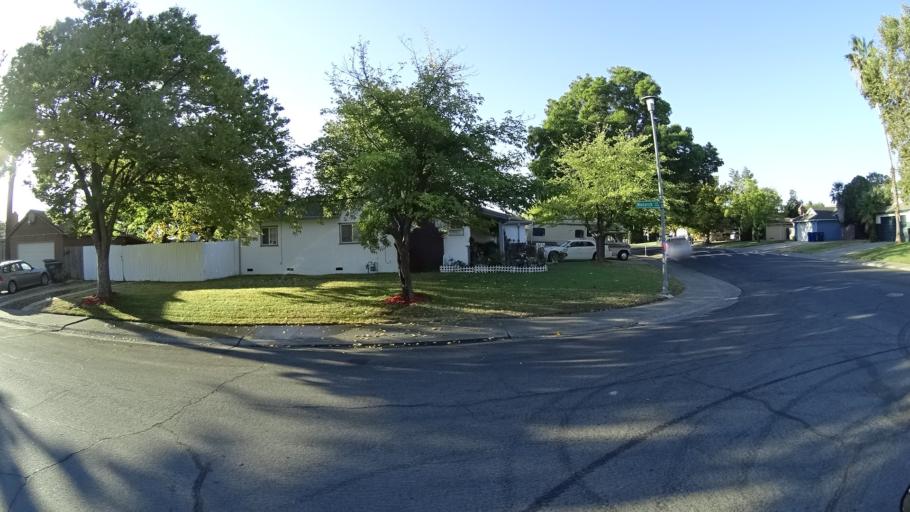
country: US
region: California
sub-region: Sacramento County
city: Parkway
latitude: 38.4789
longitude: -121.4947
